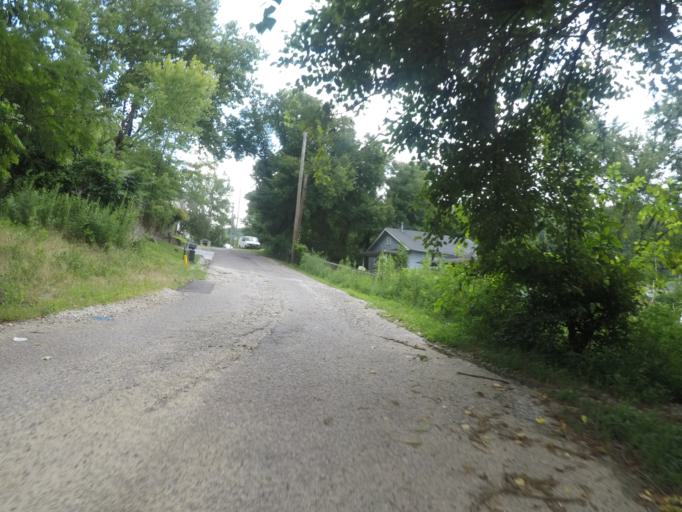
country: US
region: West Virginia
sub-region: Cabell County
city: Huntington
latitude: 38.4206
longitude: -82.3839
